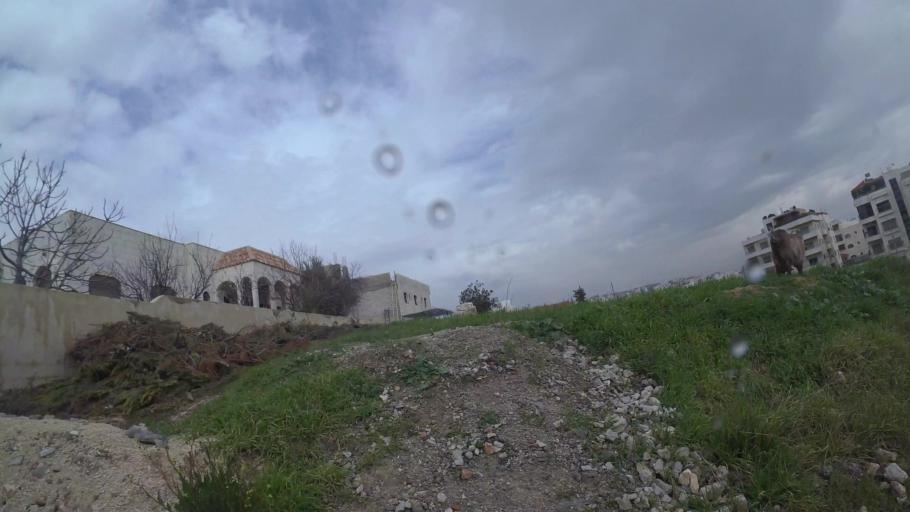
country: JO
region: Amman
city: Umm as Summaq
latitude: 31.9087
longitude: 35.8515
